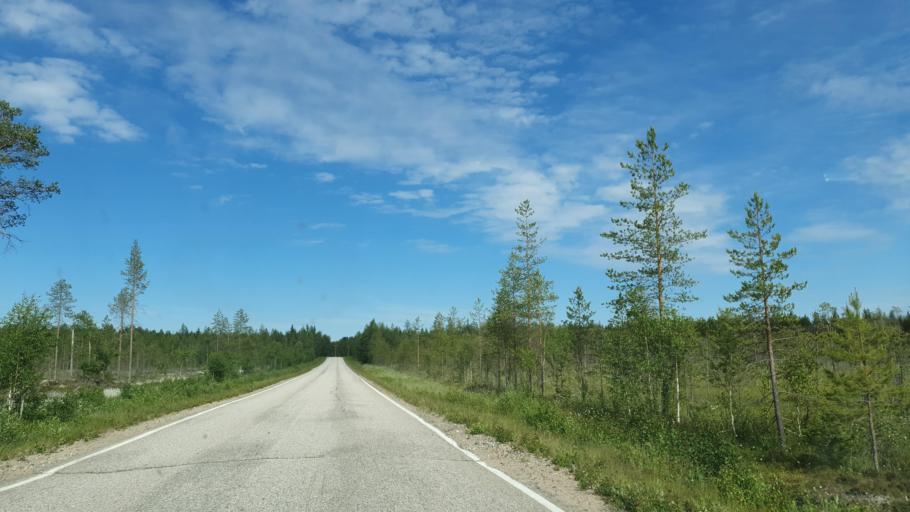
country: FI
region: Kainuu
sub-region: Kehys-Kainuu
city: Suomussalmi
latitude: 64.5684
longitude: 28.9854
